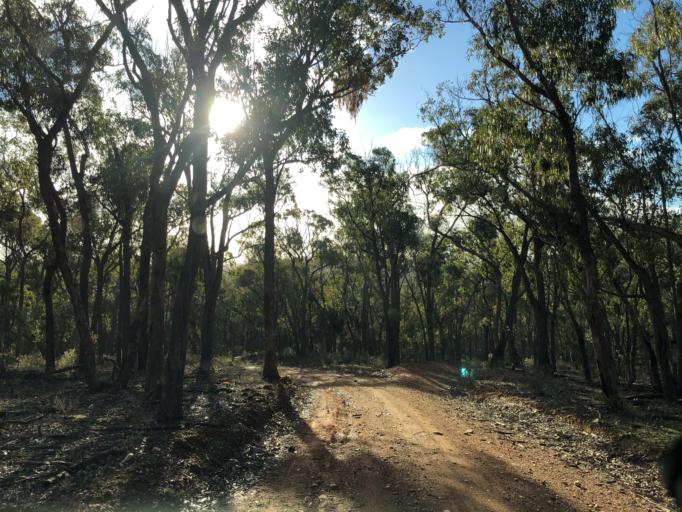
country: AU
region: Victoria
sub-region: Mount Alexander
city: Castlemaine
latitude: -37.2254
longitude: 144.2674
